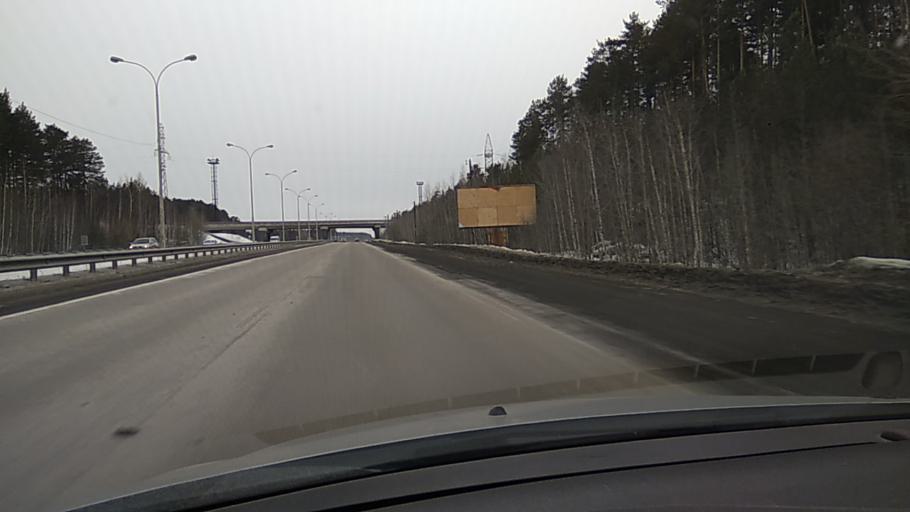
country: RU
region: Sverdlovsk
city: Shirokaya Rechka
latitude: 56.8260
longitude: 60.4954
